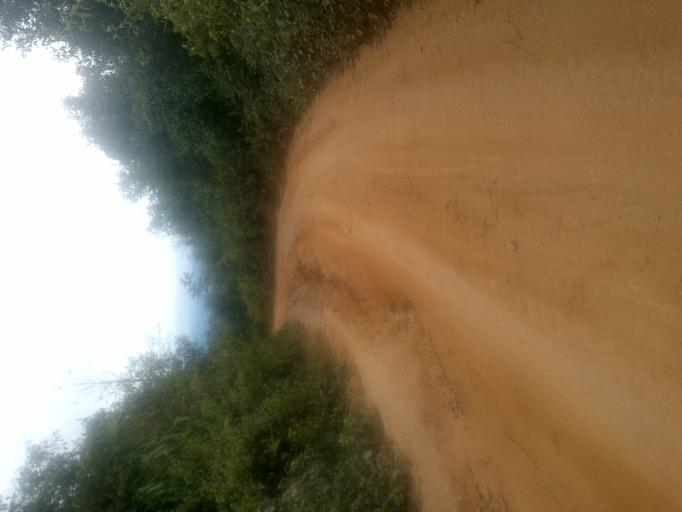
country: LA
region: Xiangkhoang
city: Muang Phonsavan
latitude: 19.3379
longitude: 103.5026
